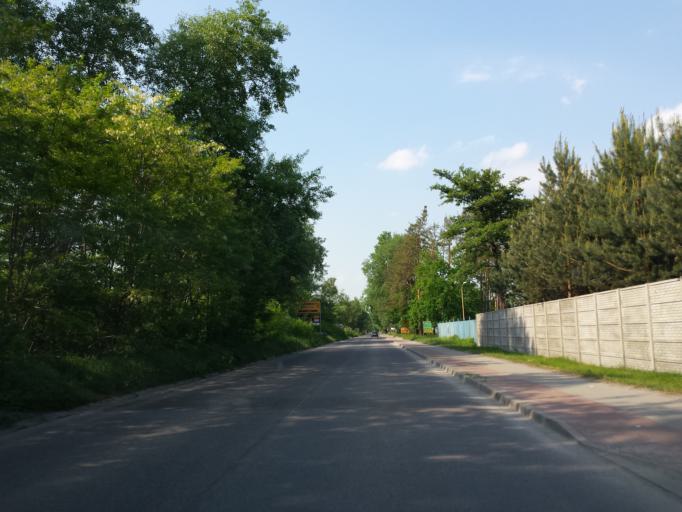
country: SK
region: Bratislavsky
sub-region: Okres Malacky
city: Malacky
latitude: 48.4145
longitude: 17.0205
